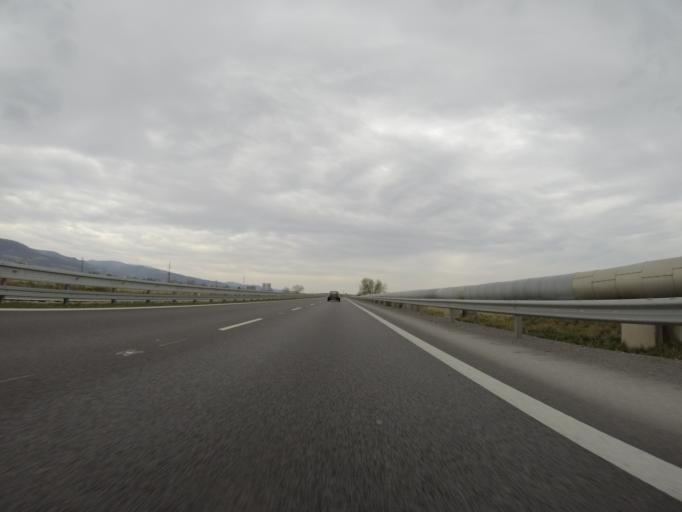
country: SK
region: Nitriansky
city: Prievidza
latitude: 48.7422
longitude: 18.6186
